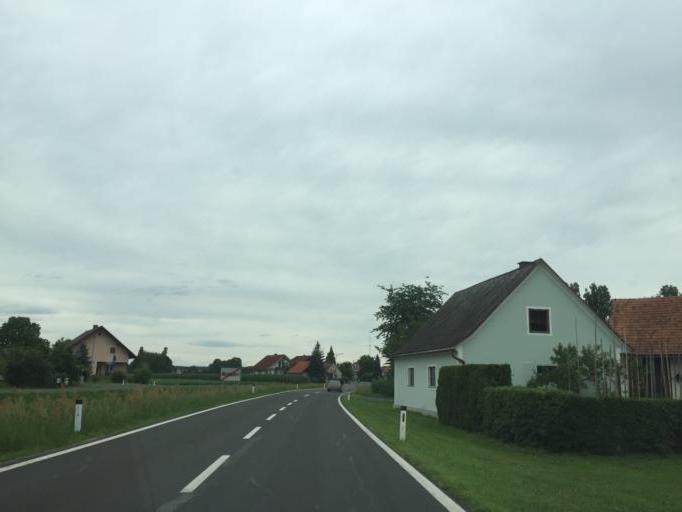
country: AT
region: Styria
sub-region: Politischer Bezirk Suedoststeiermark
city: Gosdorf
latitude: 46.7165
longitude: 15.7943
